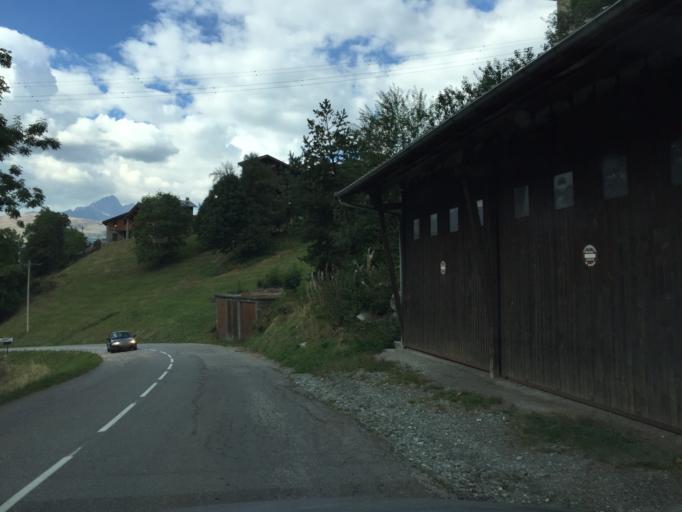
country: FR
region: Rhone-Alpes
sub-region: Departement de la Savoie
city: Belle-Plagne
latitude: 45.5447
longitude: 6.7555
